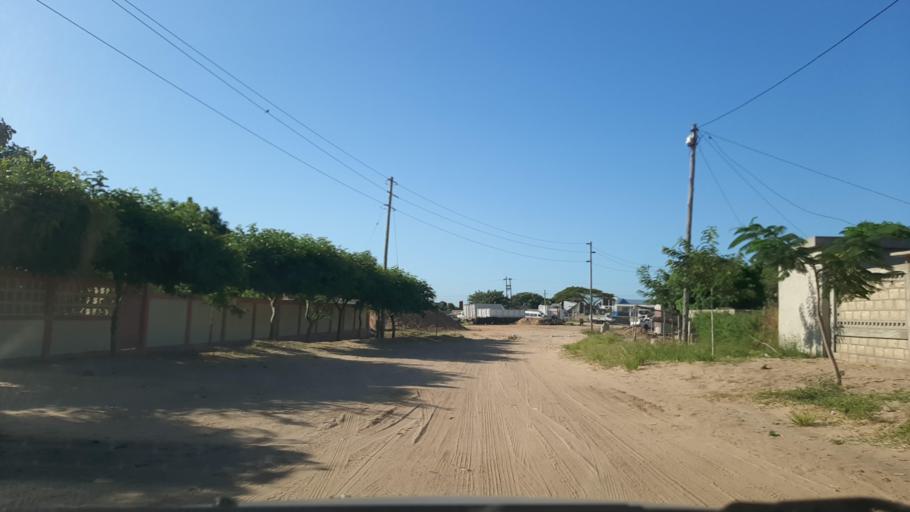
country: MZ
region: Maputo City
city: Maputo
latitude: -25.7543
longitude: 32.5502
